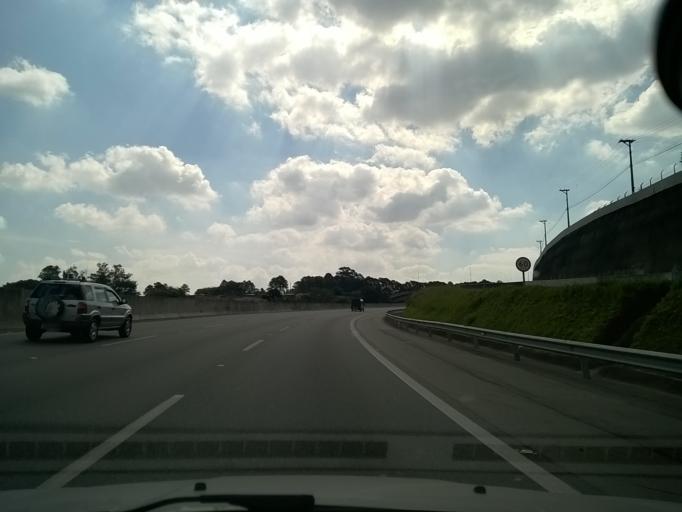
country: BR
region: Sao Paulo
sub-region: Osasco
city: Osasco
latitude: -23.5065
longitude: -46.7510
